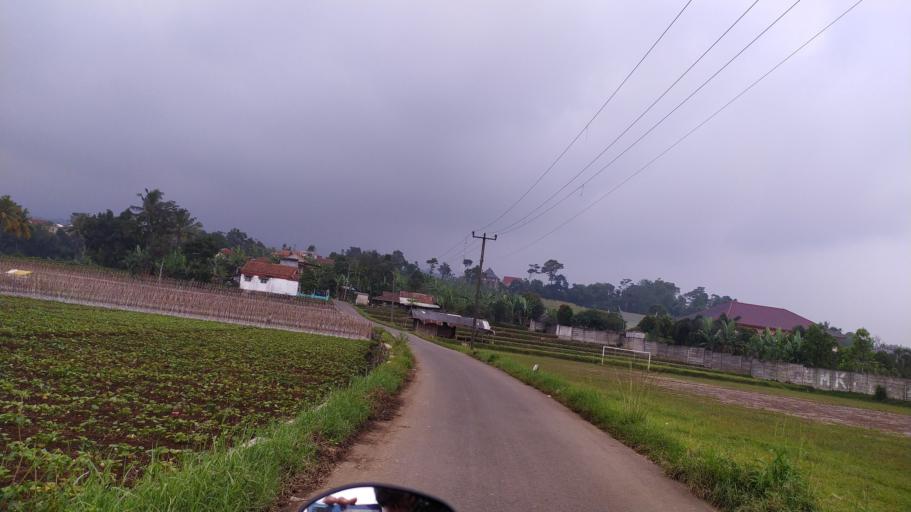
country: ID
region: West Java
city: Ciampea
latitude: -6.6345
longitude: 106.7069
